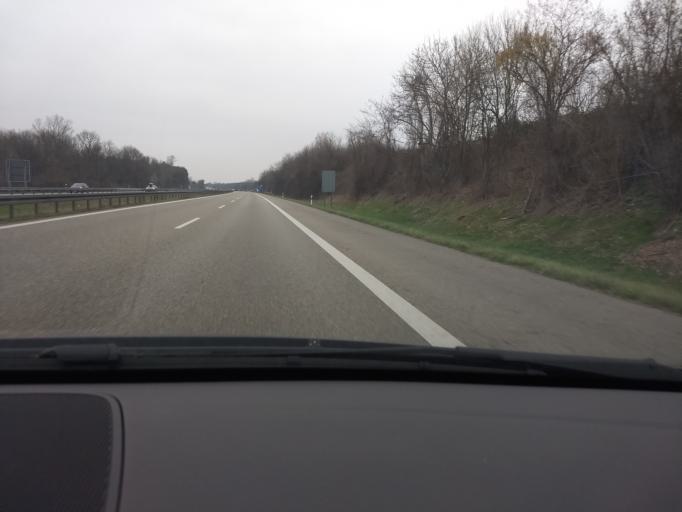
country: DE
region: Baden-Wuerttemberg
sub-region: Freiburg Region
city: Neuenburg am Rhein
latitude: 47.8248
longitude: 7.5606
